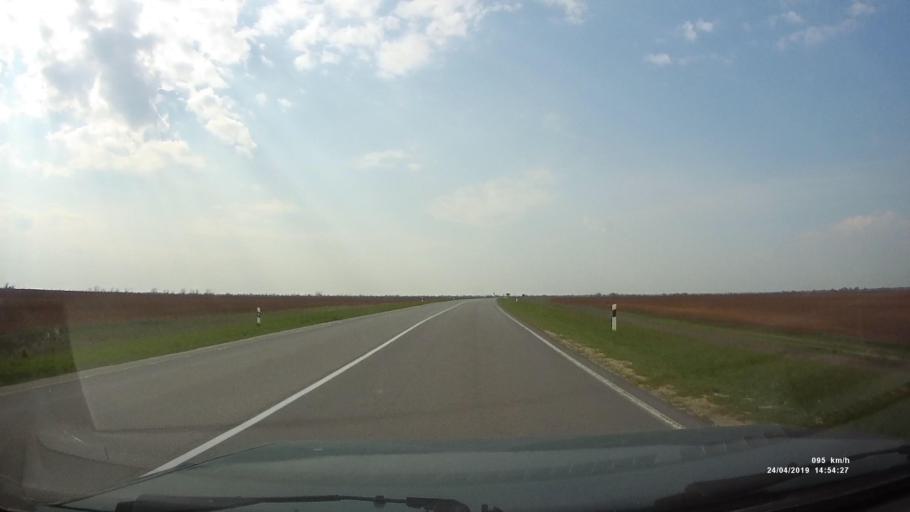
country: RU
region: Rostov
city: Remontnoye
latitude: 46.5343
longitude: 43.6389
